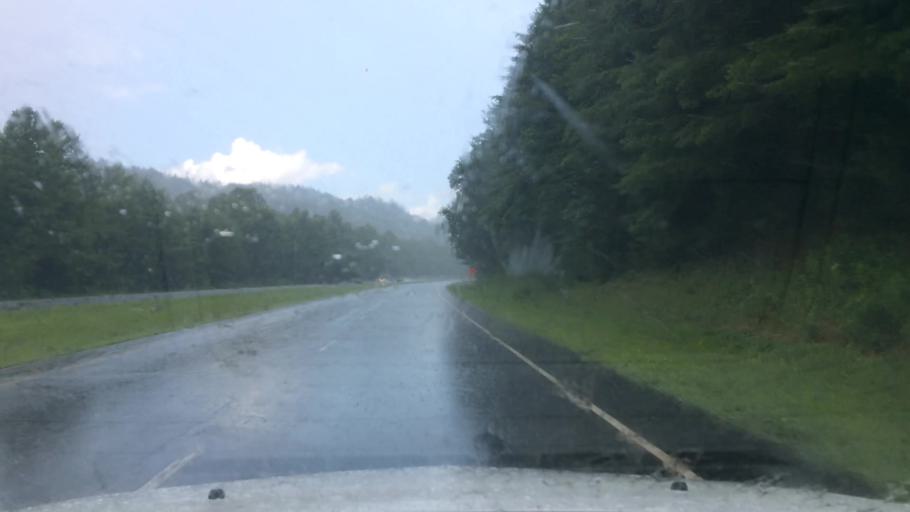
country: US
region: North Carolina
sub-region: Wilkes County
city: Millers Creek
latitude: 36.1954
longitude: -81.4242
